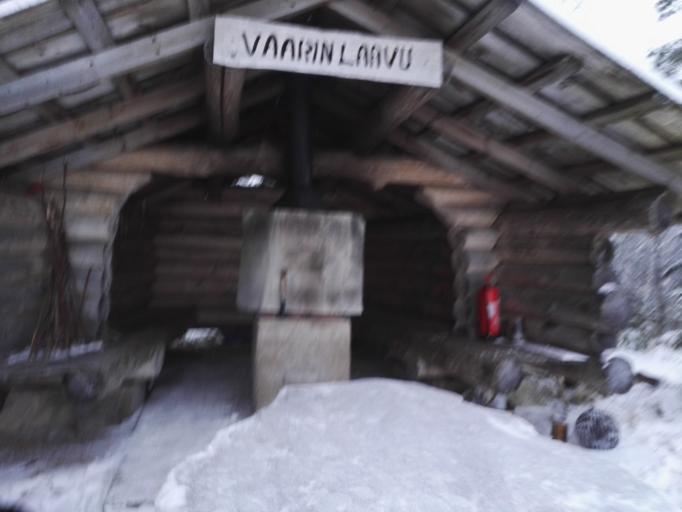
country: FI
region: Satakunta
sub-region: Pohjois-Satakunta
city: Jaemijaervi
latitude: 61.7850
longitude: 22.8709
